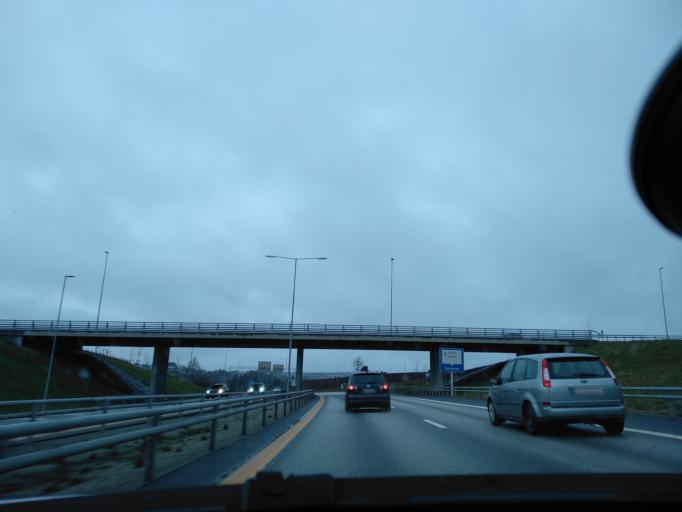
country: NO
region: Rogaland
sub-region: Sandnes
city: Sandnes
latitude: 58.8348
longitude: 5.7362
